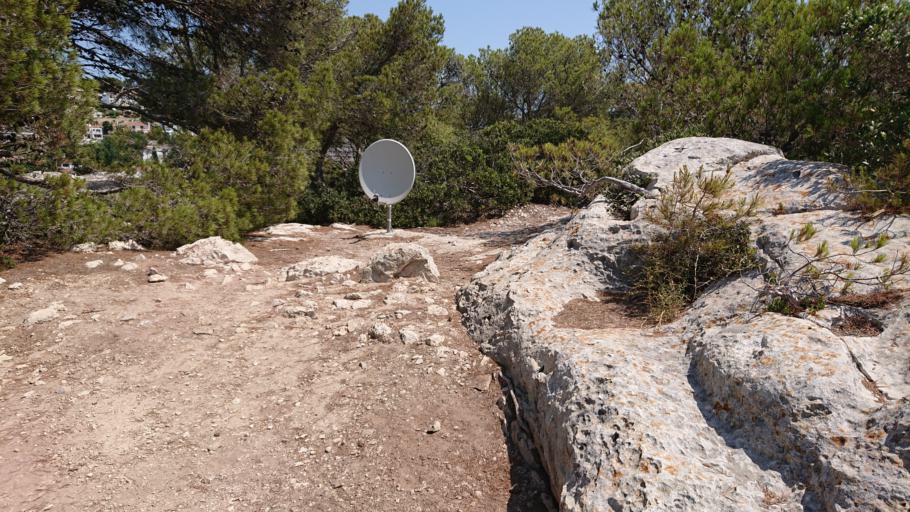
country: ES
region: Balearic Islands
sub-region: Illes Balears
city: Ferreries
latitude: 39.9377
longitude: 3.9579
